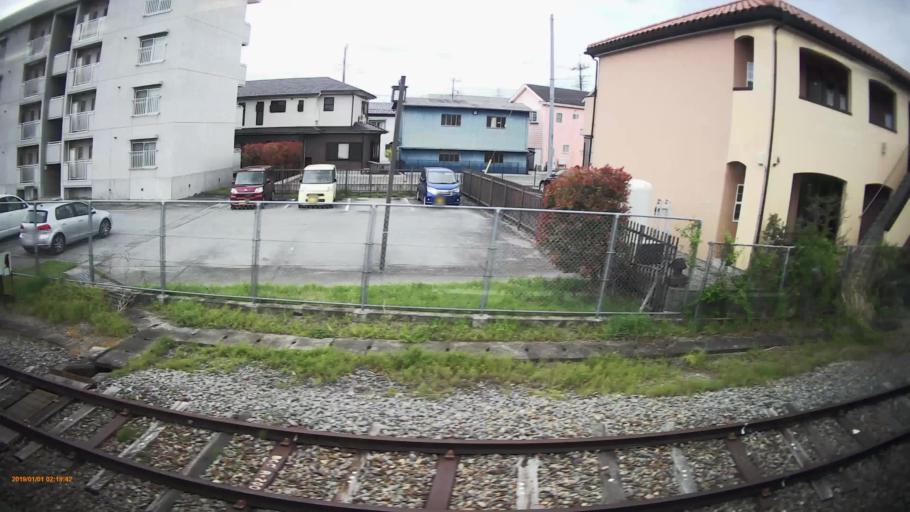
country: JP
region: Yamanashi
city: Ryuo
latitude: 35.6686
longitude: 138.5170
